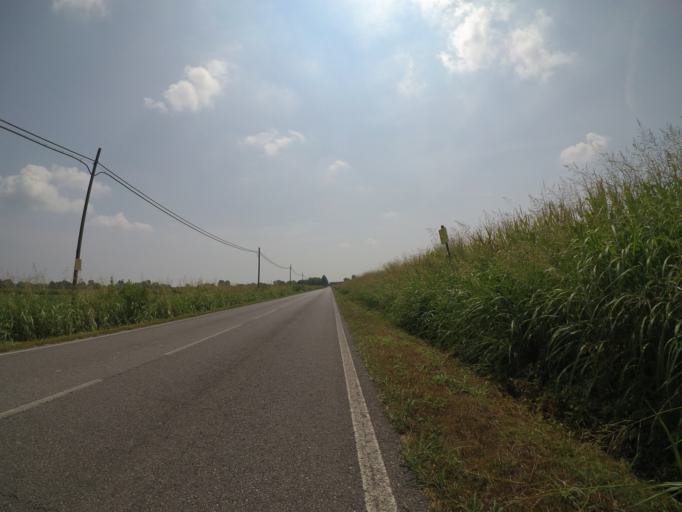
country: IT
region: Friuli Venezia Giulia
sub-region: Provincia di Udine
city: Teor
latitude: 45.8433
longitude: 13.0760
